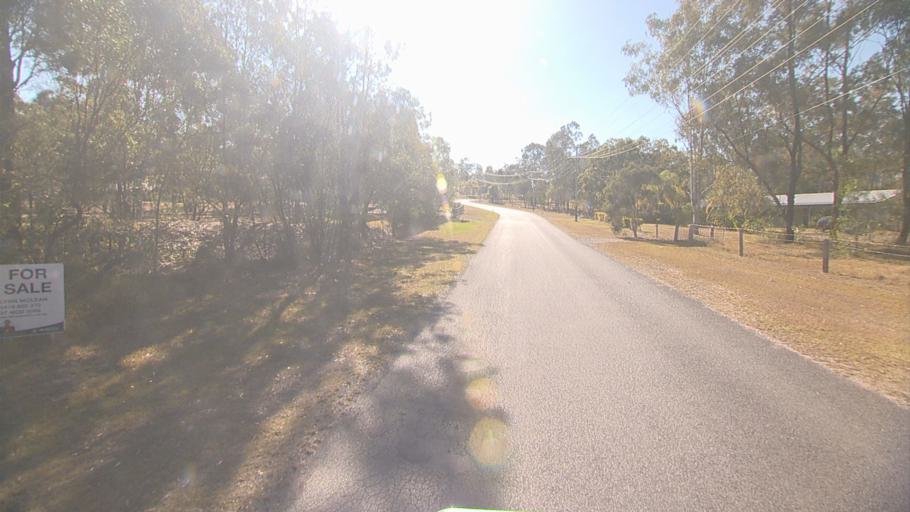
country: AU
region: Queensland
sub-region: Logan
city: Cedar Vale
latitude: -27.8301
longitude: 153.0436
